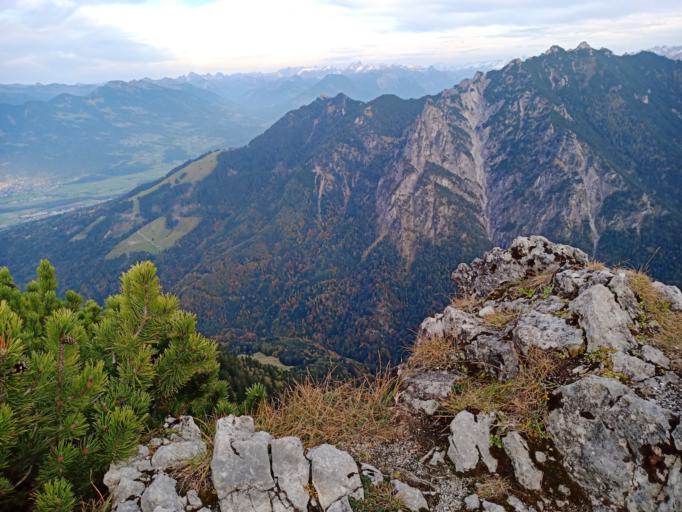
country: LI
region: Planken
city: Planken
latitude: 47.1781
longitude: 9.5742
